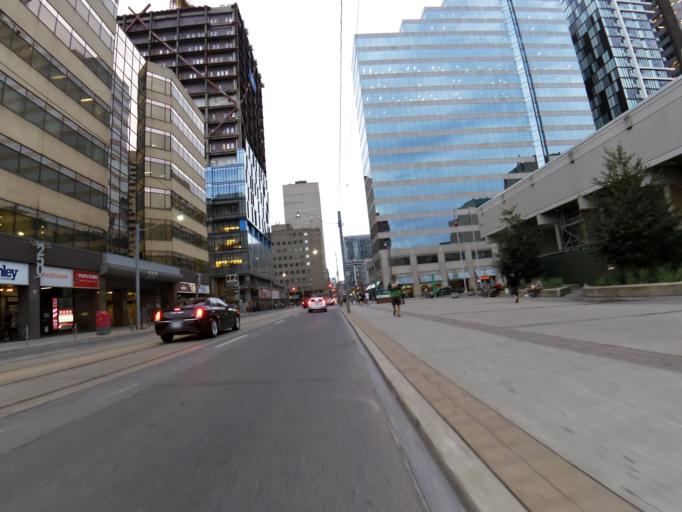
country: CA
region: Ontario
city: Toronto
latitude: 43.6545
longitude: -79.3900
